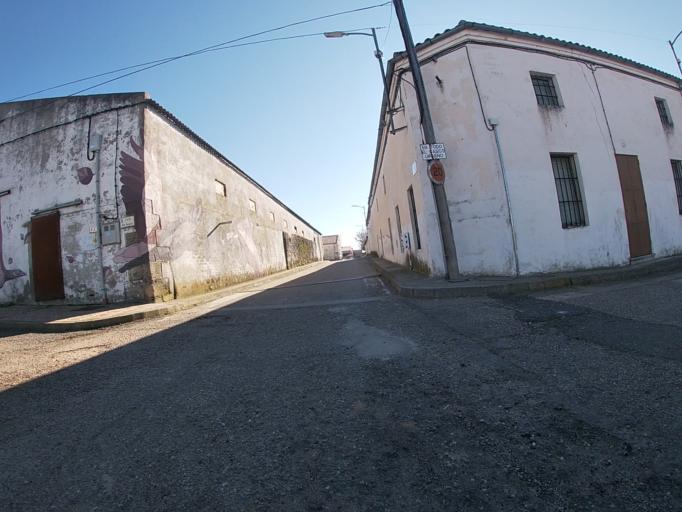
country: ES
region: Castille and Leon
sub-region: Provincia de Salamanca
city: Juzbado
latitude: 41.0784
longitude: -5.8615
